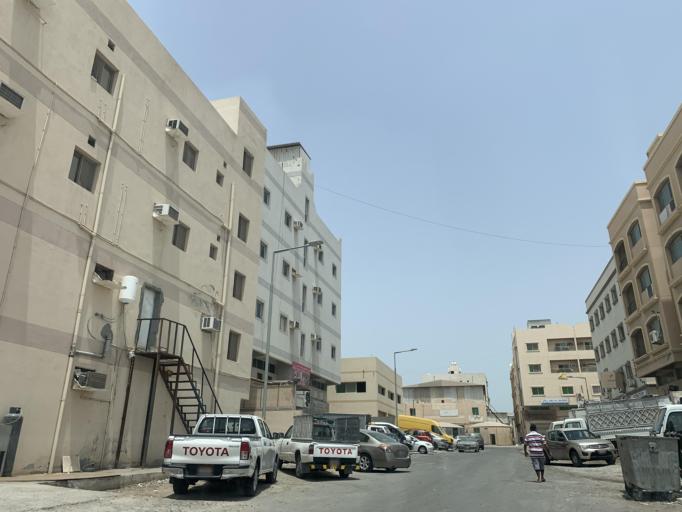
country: BH
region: Northern
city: Ar Rifa'
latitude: 26.1369
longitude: 50.5870
